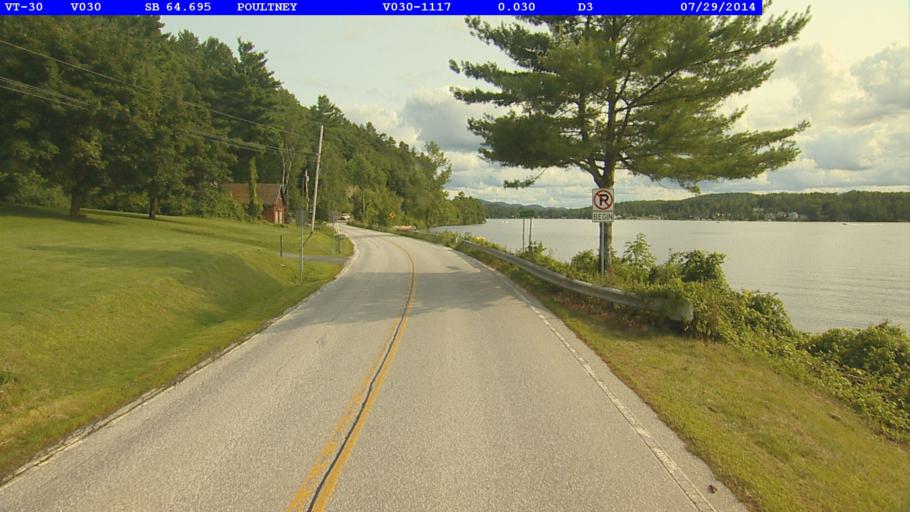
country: US
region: Vermont
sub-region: Rutland County
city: Poultney
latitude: 43.4645
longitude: -73.2059
